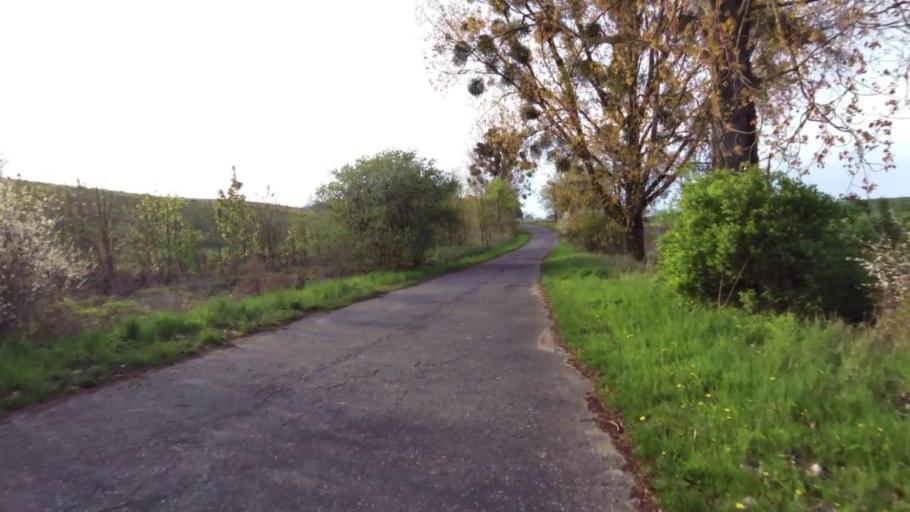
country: PL
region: West Pomeranian Voivodeship
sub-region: Powiat mysliborski
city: Mysliborz
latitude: 52.8959
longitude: 14.7752
